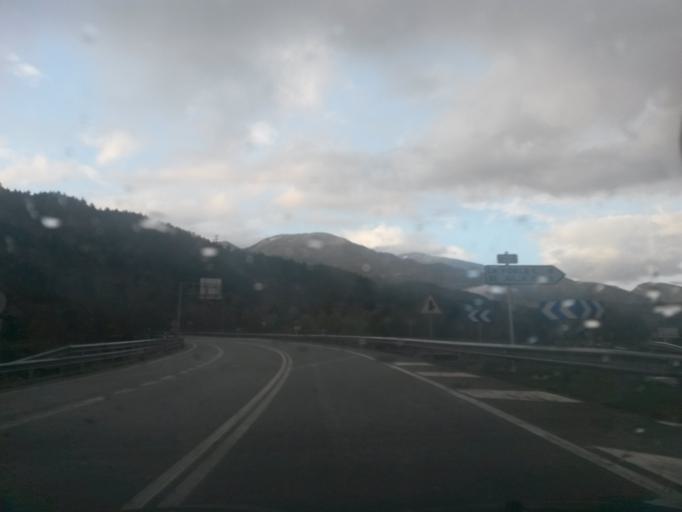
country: ES
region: Catalonia
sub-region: Provincia de Barcelona
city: Guardiola de Bergueda
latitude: 42.2316
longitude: 1.8838
